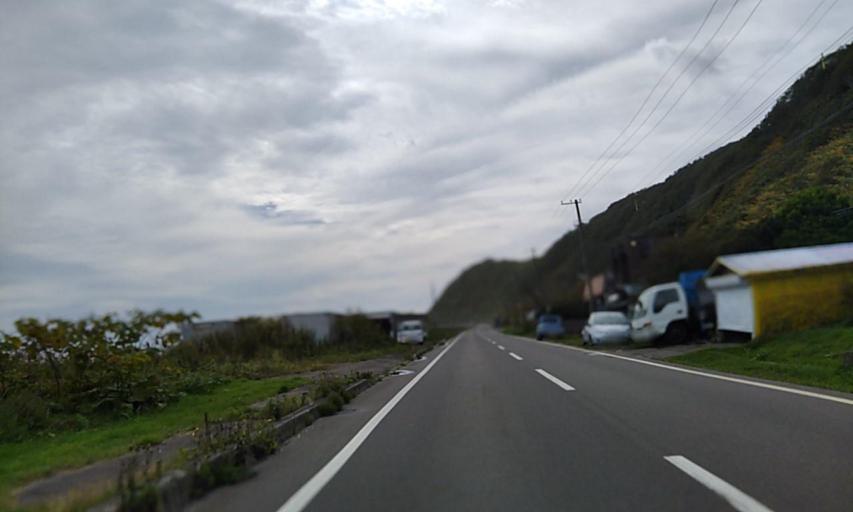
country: JP
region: Hokkaido
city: Kushiro
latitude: 42.7970
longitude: 143.8079
